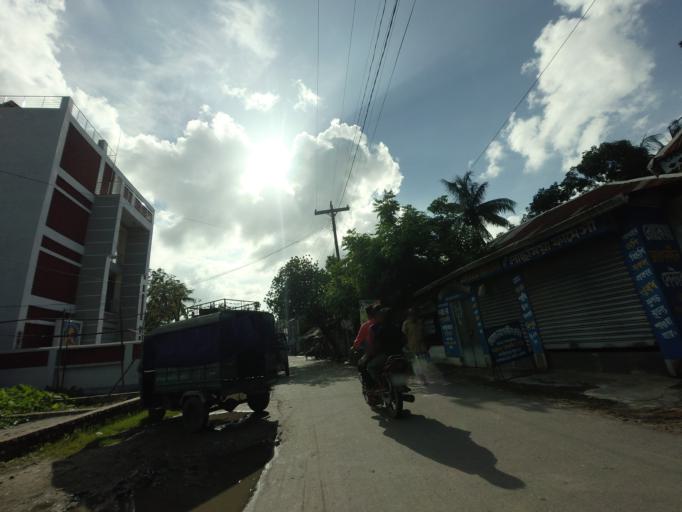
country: BD
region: Khulna
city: Kalia
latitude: 23.0411
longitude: 89.6328
